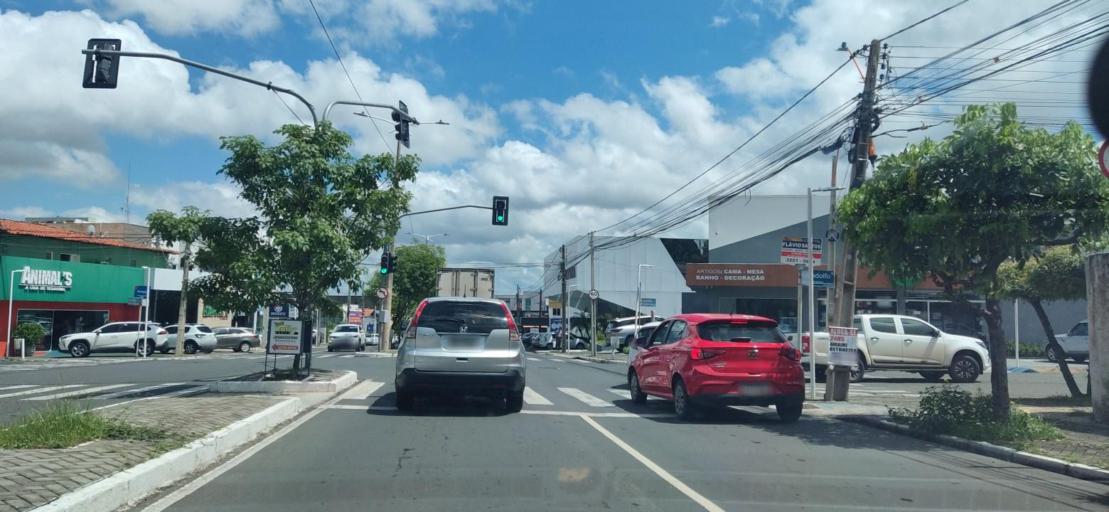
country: BR
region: Piaui
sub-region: Teresina
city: Teresina
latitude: -5.0676
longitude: -42.7931
